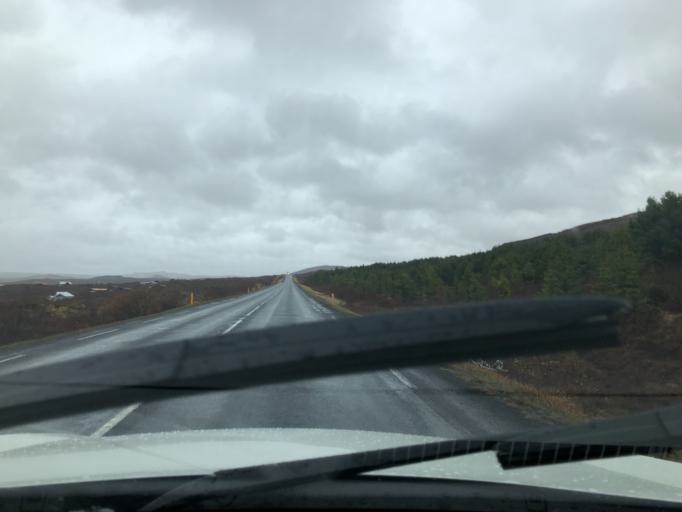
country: IS
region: South
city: Selfoss
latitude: 64.0343
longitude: -20.9000
